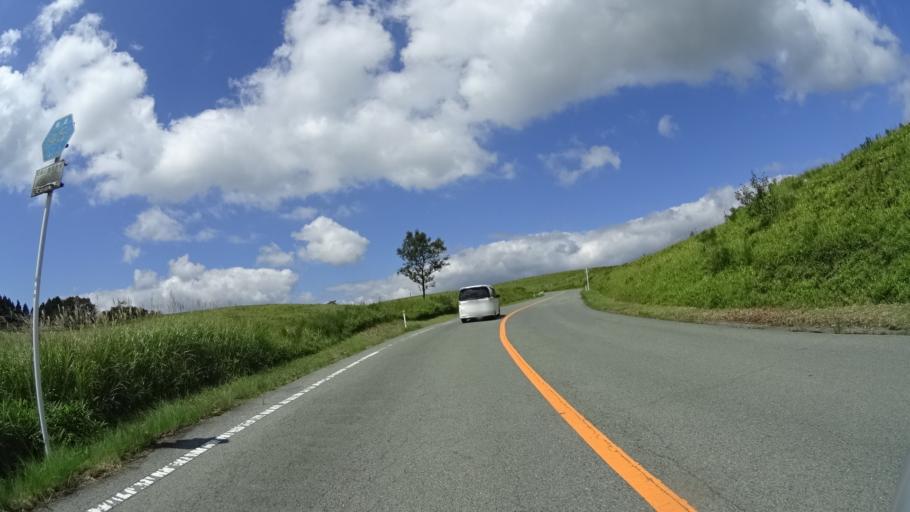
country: JP
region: Kumamoto
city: Aso
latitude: 33.0017
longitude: 131.1349
